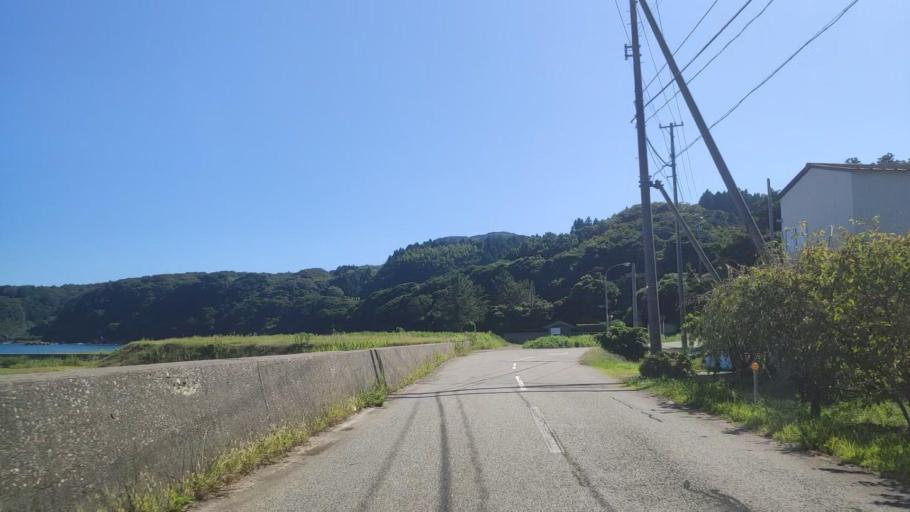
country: JP
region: Ishikawa
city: Nanao
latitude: 37.5225
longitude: 137.3265
